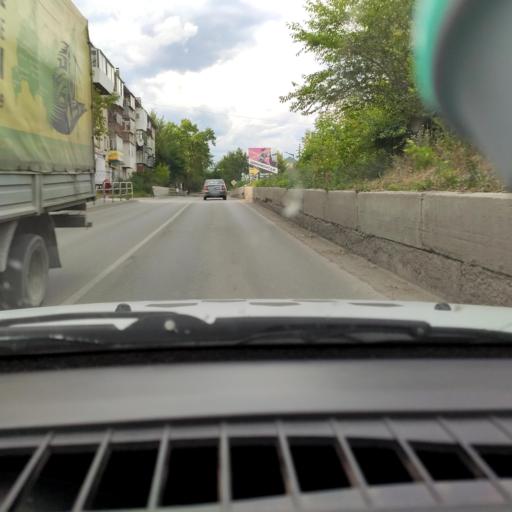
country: RU
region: Chelyabinsk
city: Miass
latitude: 55.0558
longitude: 60.1116
